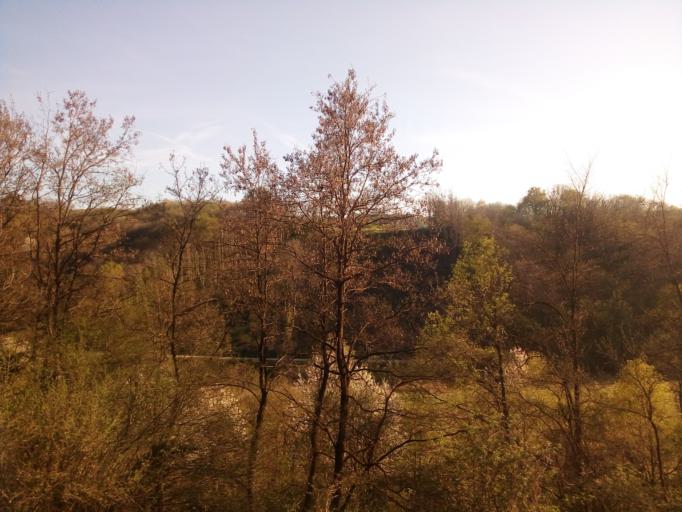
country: FR
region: Rhone-Alpes
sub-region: Departement de l'Isere
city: Saint-Didier-de-la-Tour
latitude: 45.5567
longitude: 5.5056
